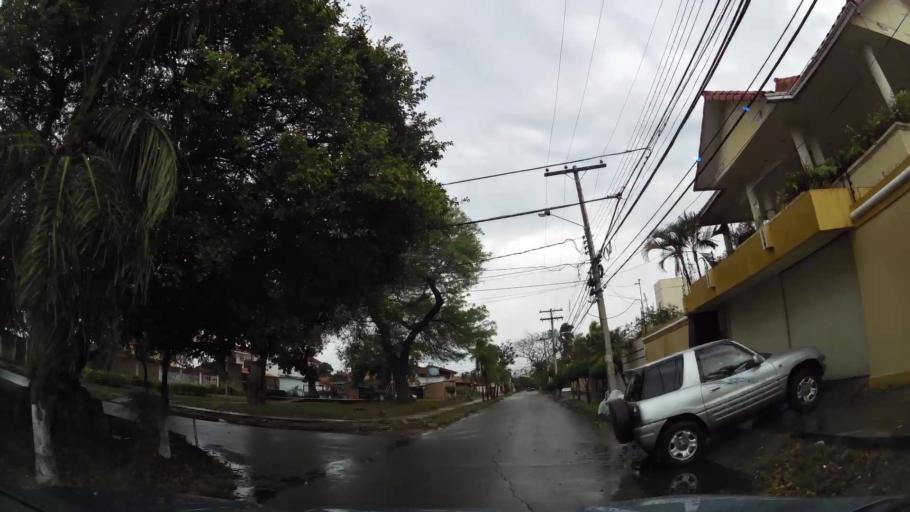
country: BO
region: Santa Cruz
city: Santa Cruz de la Sierra
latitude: -17.7666
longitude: -63.1542
